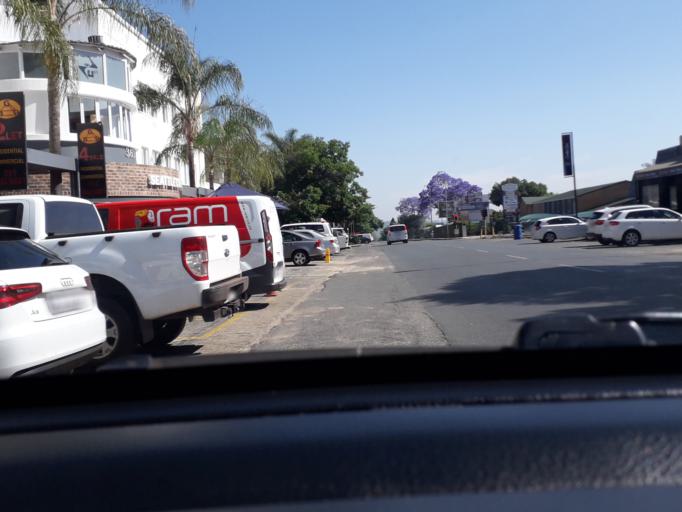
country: ZA
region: Gauteng
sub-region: City of Johannesburg Metropolitan Municipality
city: Midrand
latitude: -26.0524
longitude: 28.0599
